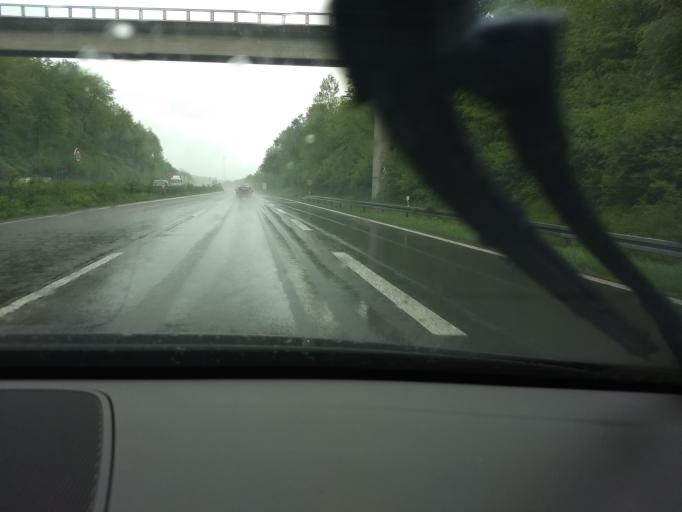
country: DE
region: North Rhine-Westphalia
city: Dorsten
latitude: 51.6569
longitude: 6.9280
